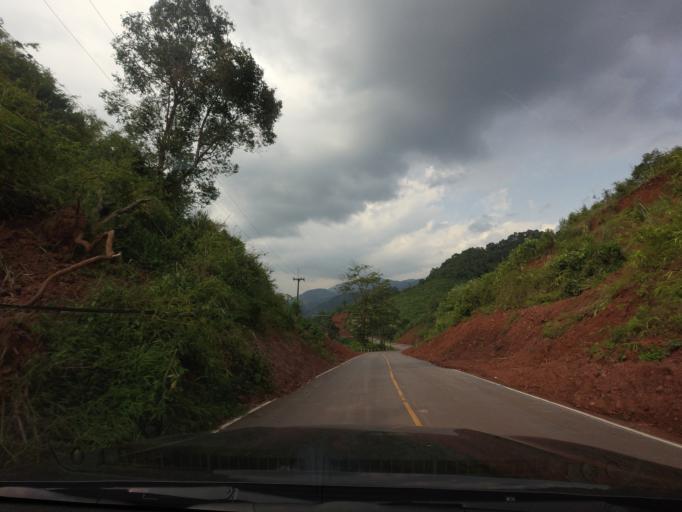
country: TH
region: Nan
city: Bo Kluea
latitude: 19.2607
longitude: 101.1787
